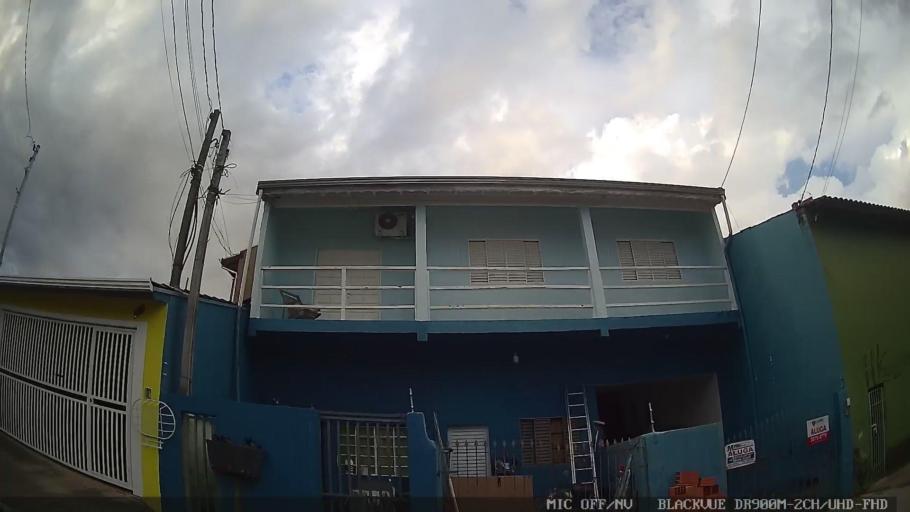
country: BR
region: Sao Paulo
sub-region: Indaiatuba
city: Indaiatuba
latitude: -23.1244
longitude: -47.2382
